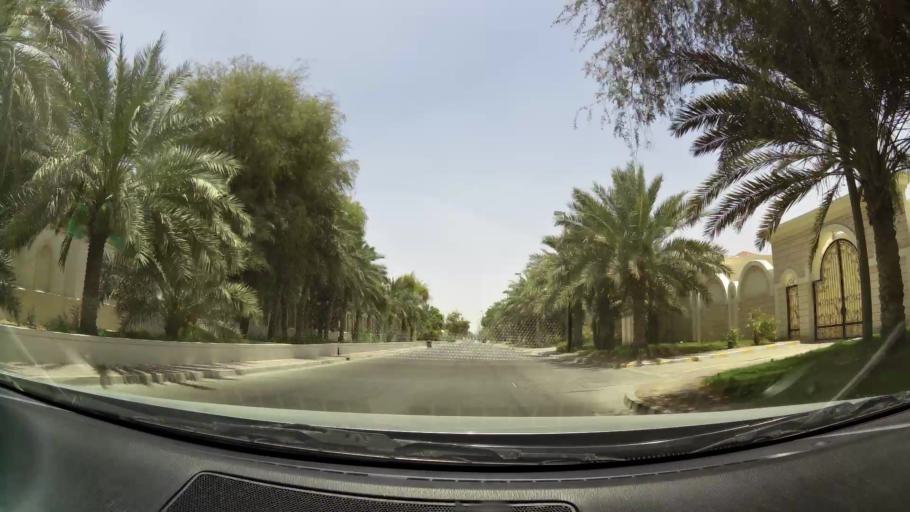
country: OM
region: Al Buraimi
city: Al Buraymi
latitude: 24.2682
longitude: 55.7367
